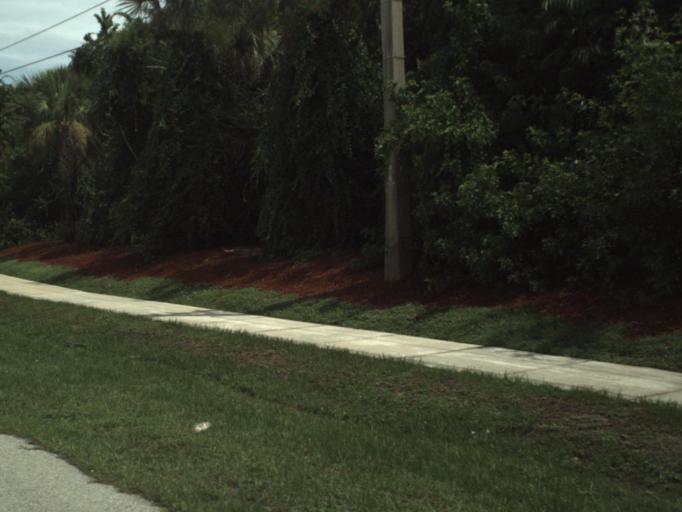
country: US
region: Florida
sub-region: Palm Beach County
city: Jupiter
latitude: 26.9283
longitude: -80.0777
